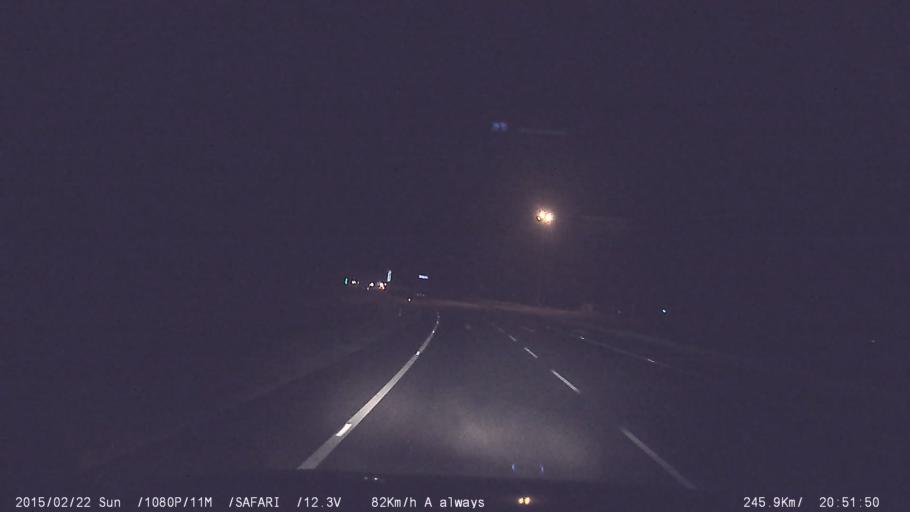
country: IN
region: Tamil Nadu
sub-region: Dindigul
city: Vedasandur
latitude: 10.5466
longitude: 77.9446
